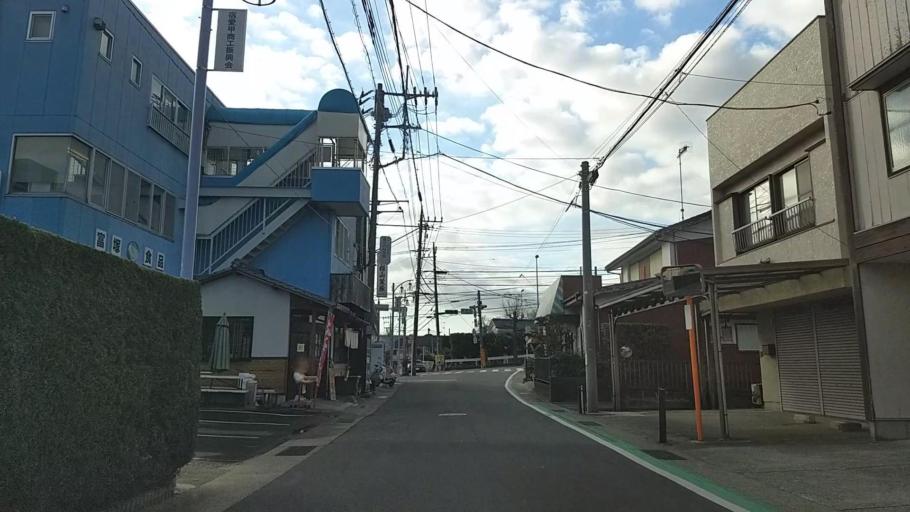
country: JP
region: Kanagawa
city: Atsugi
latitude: 35.4185
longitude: 139.3473
